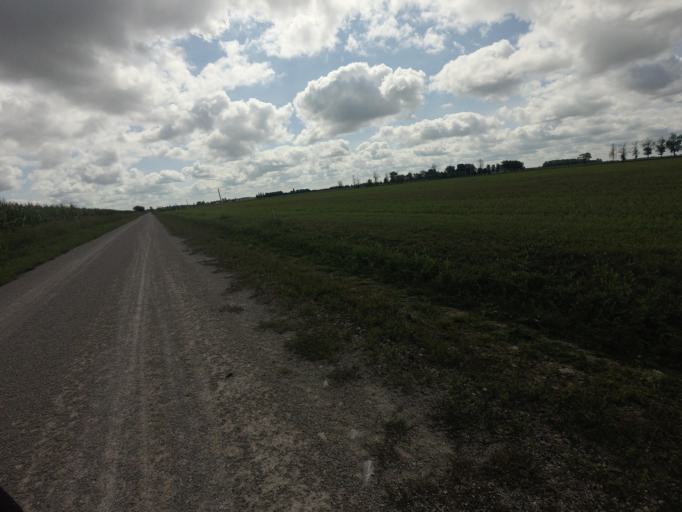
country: CA
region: Ontario
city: Huron East
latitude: 43.6108
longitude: -81.1313
